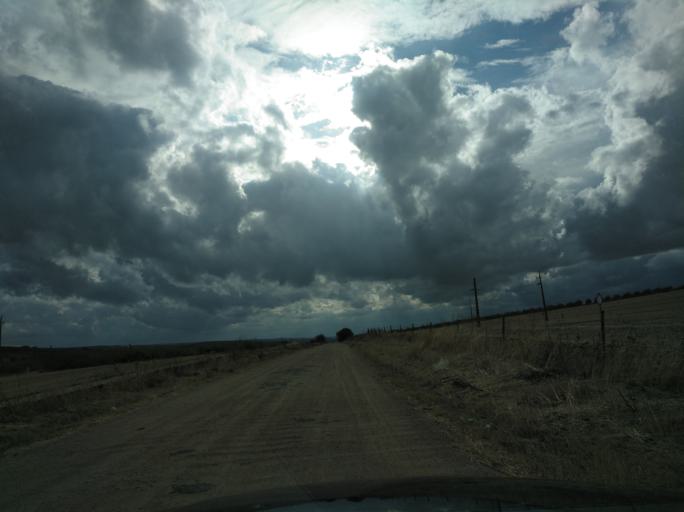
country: PT
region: Portalegre
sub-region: Campo Maior
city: Campo Maior
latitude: 39.0410
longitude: -7.1078
